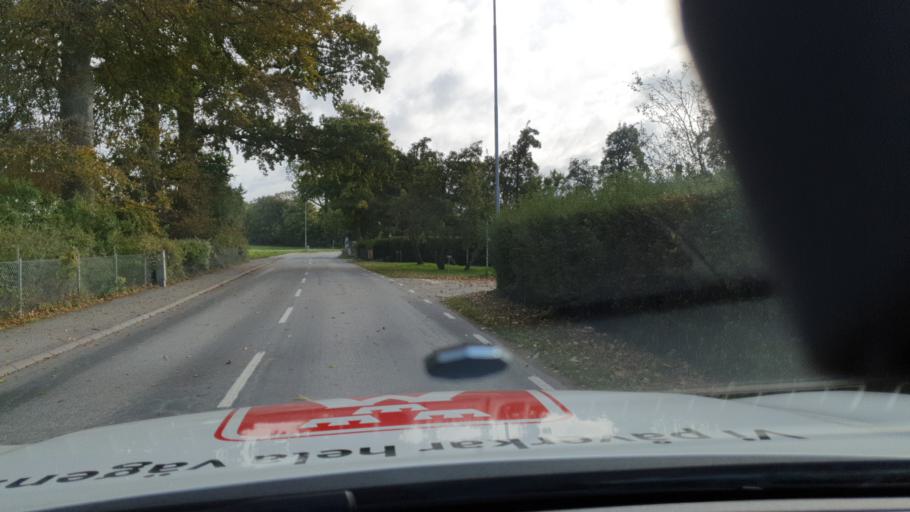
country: SE
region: Skane
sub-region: Malmo
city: Tygelsjo
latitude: 55.5042
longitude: 13.0280
